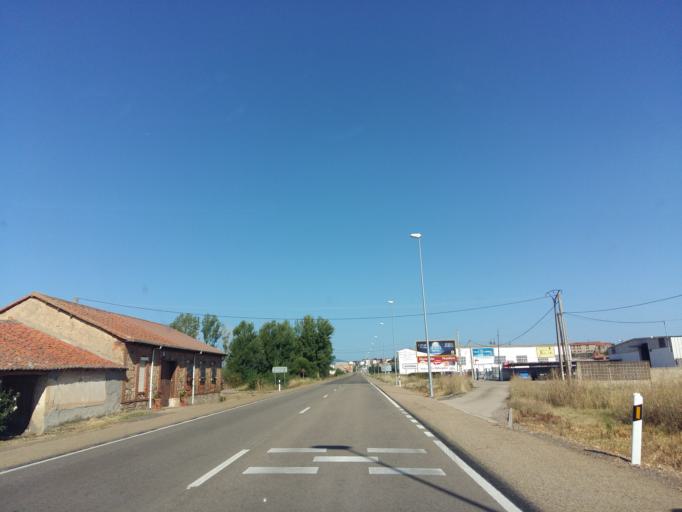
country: ES
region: Castille and Leon
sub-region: Provincia de Leon
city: Astorga
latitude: 42.4460
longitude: -6.0464
